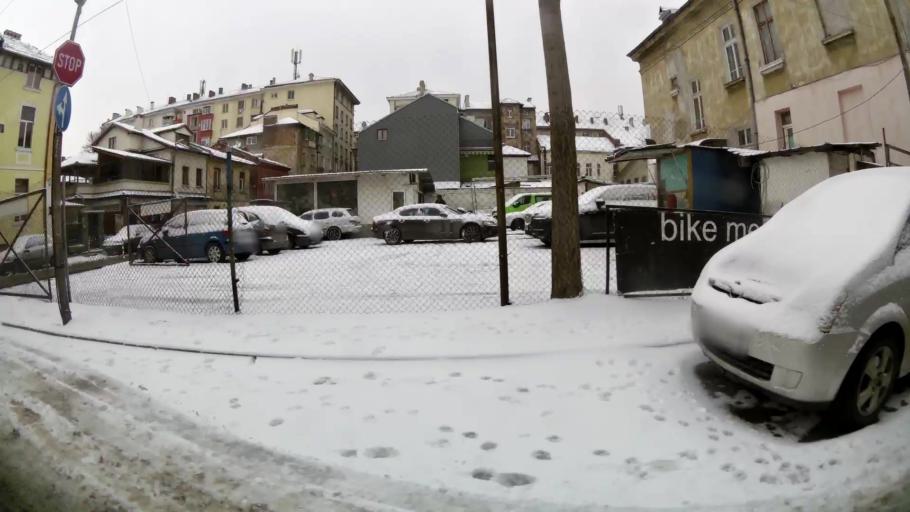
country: BG
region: Sofia-Capital
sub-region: Stolichna Obshtina
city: Sofia
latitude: 42.7029
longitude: 23.3220
